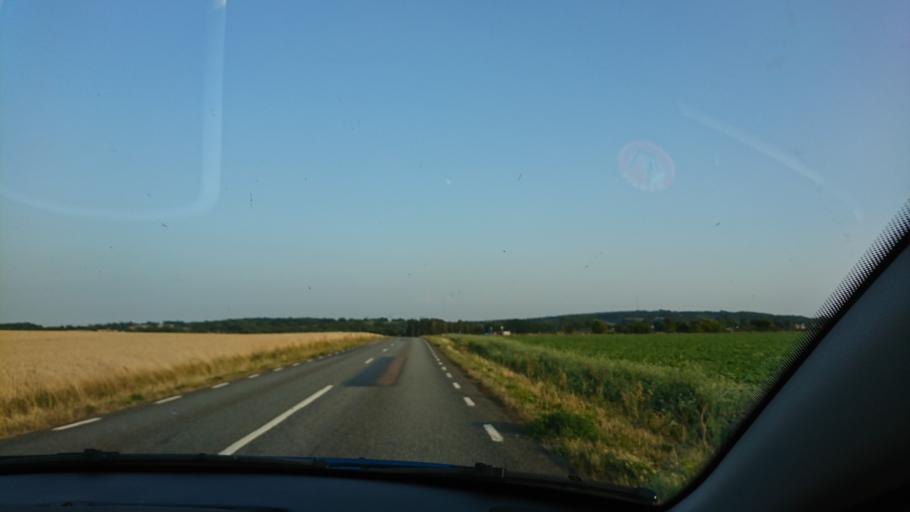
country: SE
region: Skane
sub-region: Simrishamns Kommun
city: Kivik
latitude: 55.6951
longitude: 14.1557
